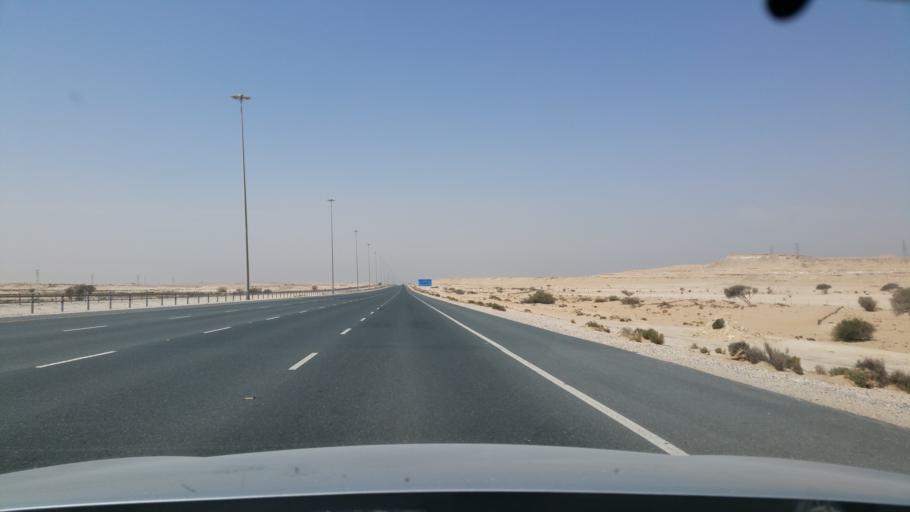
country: QA
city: Umm Bab
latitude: 24.8790
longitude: 50.9235
